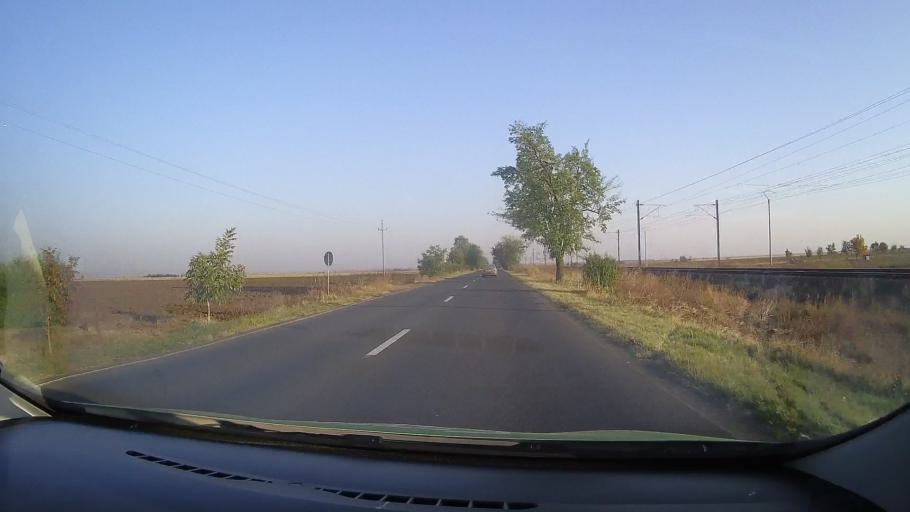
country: RO
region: Arad
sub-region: Comuna Sofronea
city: Sofronea
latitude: 46.2876
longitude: 21.3125
